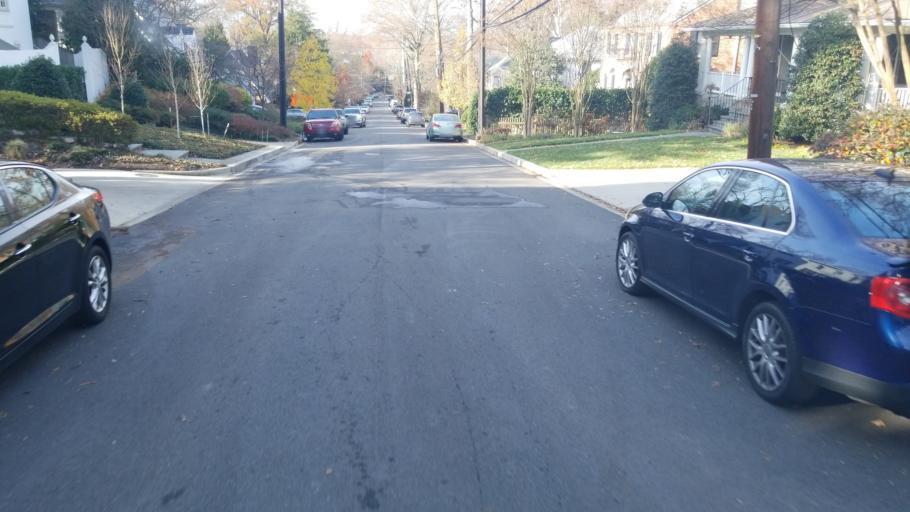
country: US
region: Maryland
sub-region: Montgomery County
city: Brookmont
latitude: 38.9315
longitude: -77.1010
